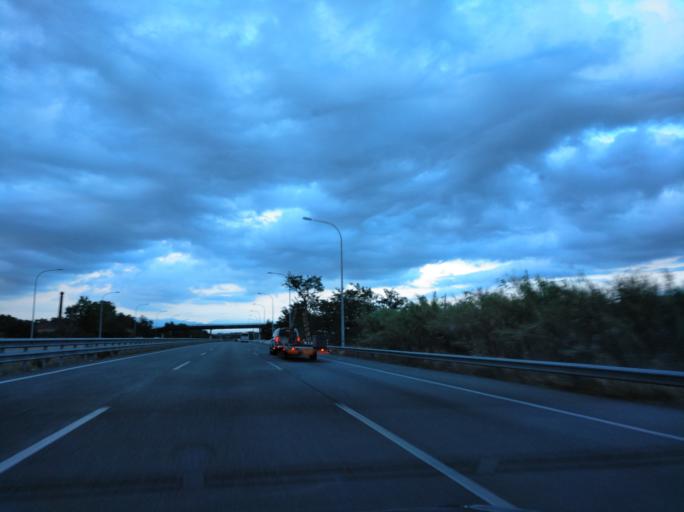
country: ES
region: Catalonia
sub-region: Provincia de Barcelona
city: Mollet del Valles
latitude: 41.5305
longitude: 2.2190
